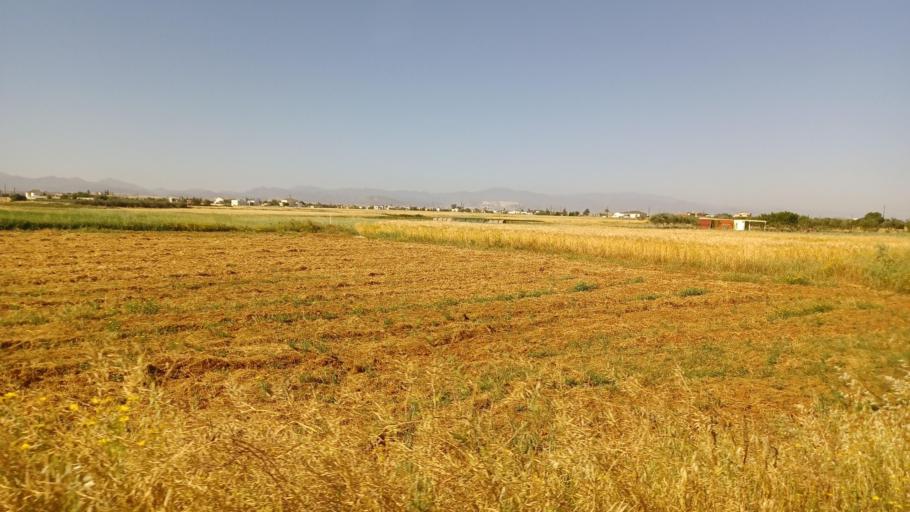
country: CY
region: Lefkosia
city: Kokkinotrimithia
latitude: 35.1438
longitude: 33.2160
